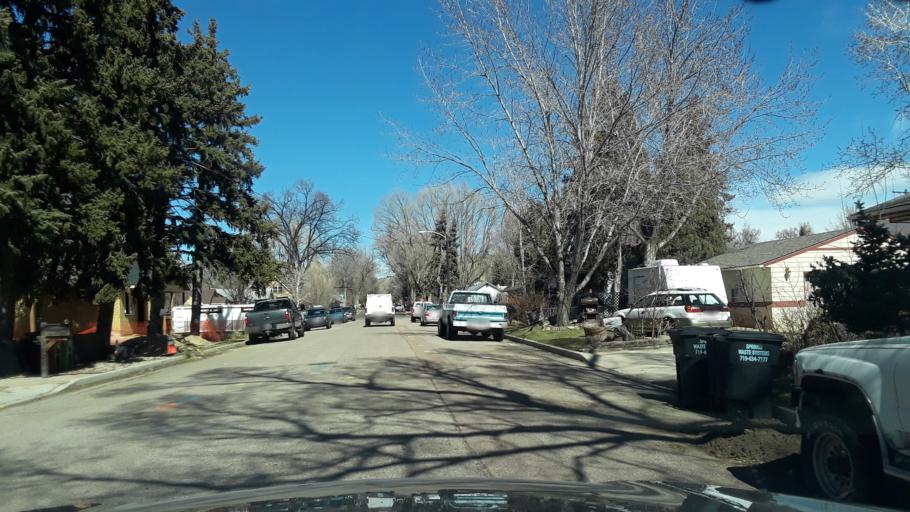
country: US
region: Colorado
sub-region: El Paso County
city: Colorado Springs
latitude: 38.8751
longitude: -104.8055
